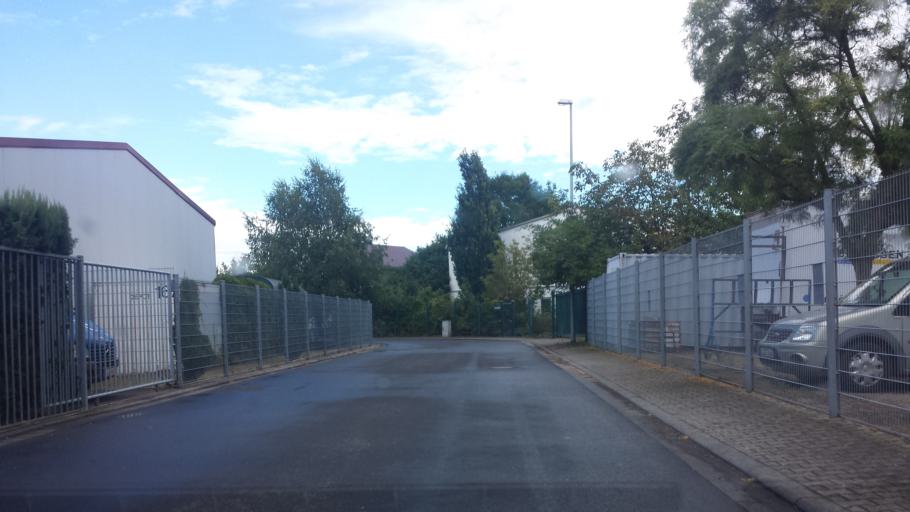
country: DE
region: Rheinland-Pfalz
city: Osthofen
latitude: 49.6984
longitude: 8.3350
